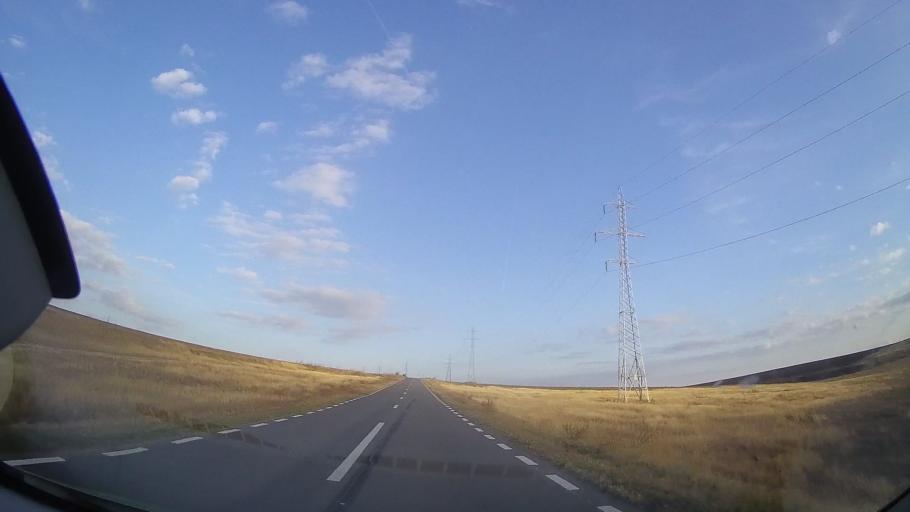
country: RO
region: Constanta
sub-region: Comuna Chirnogeni
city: Plopeni
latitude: 43.9536
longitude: 28.1529
